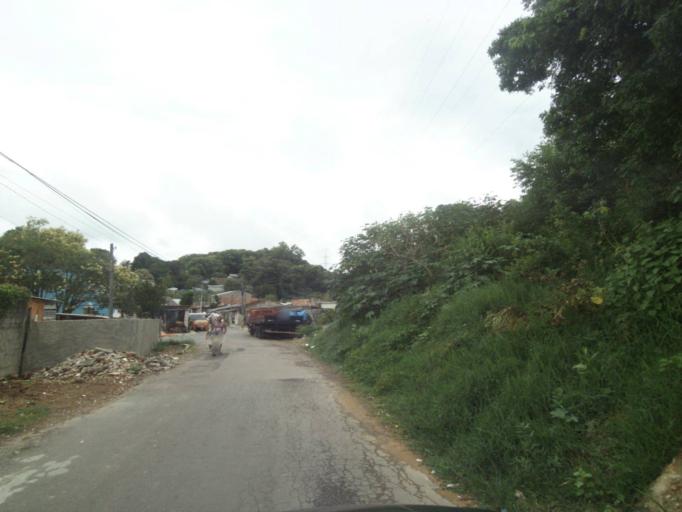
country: BR
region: Parana
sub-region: Curitiba
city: Curitiba
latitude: -25.4698
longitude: -49.3250
